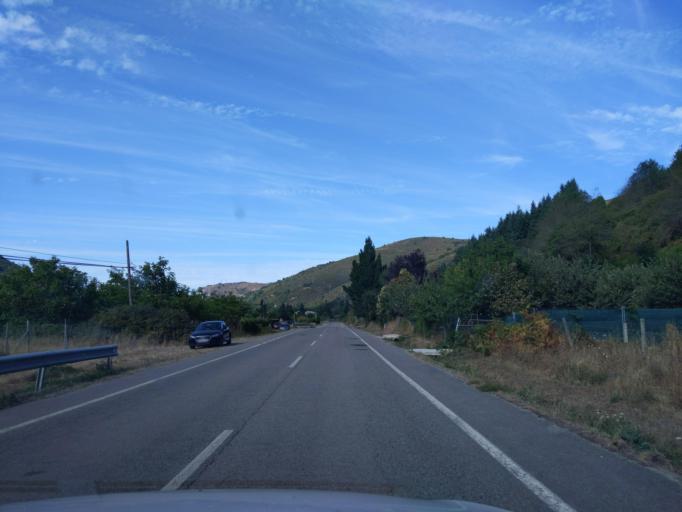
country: ES
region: La Rioja
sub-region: Provincia de La Rioja
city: Ezcaray
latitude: 42.3080
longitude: -3.0189
